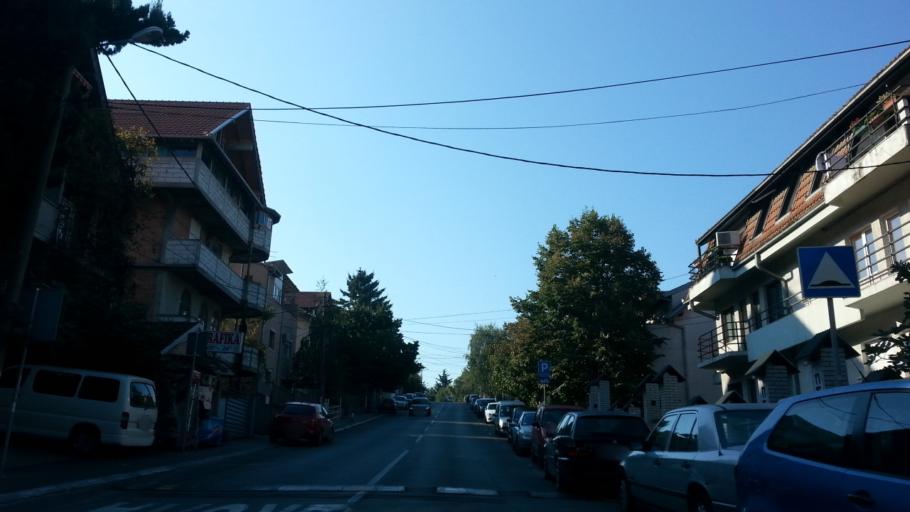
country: RS
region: Central Serbia
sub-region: Belgrade
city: Cukarica
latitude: 44.7639
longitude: 20.4191
